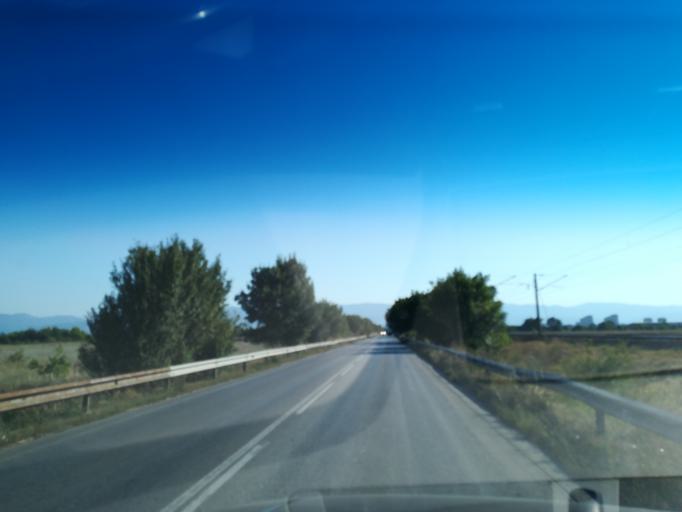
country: BG
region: Plovdiv
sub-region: Obshtina Plovdiv
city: Plovdiv
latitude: 42.1706
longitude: 24.8185
